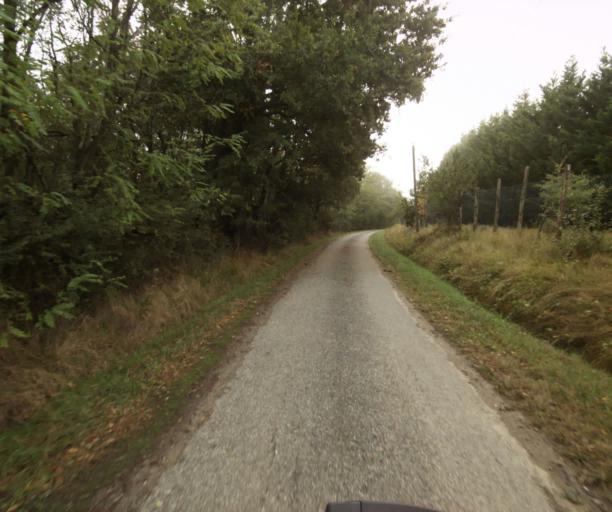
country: FR
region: Midi-Pyrenees
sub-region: Departement du Tarn-et-Garonne
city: Saint-Nauphary
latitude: 43.9351
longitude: 1.4613
